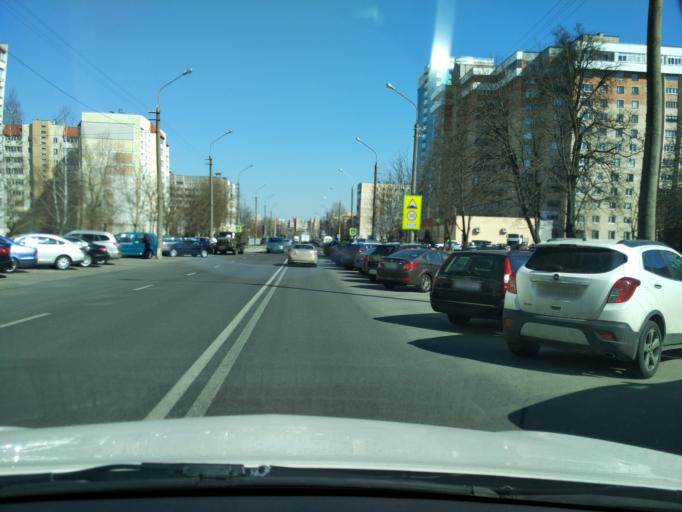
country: BY
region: Minsk
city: Minsk
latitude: 53.8776
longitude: 27.5522
